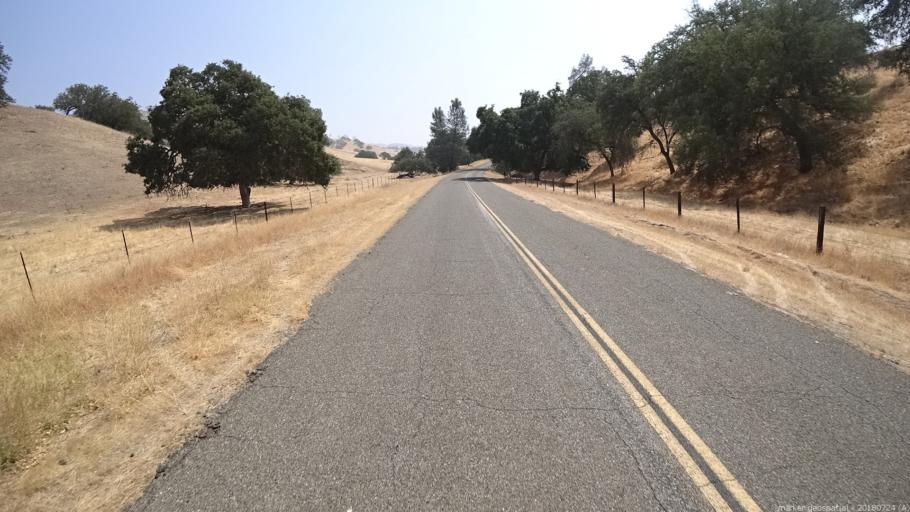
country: US
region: California
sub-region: Monterey County
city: King City
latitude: 36.1678
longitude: -120.7814
